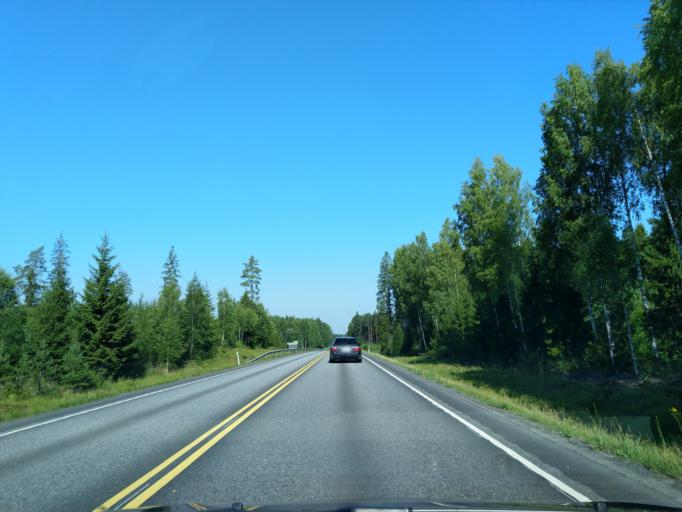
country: FI
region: Satakunta
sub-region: Pori
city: Huittinen
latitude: 61.1391
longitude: 22.7671
